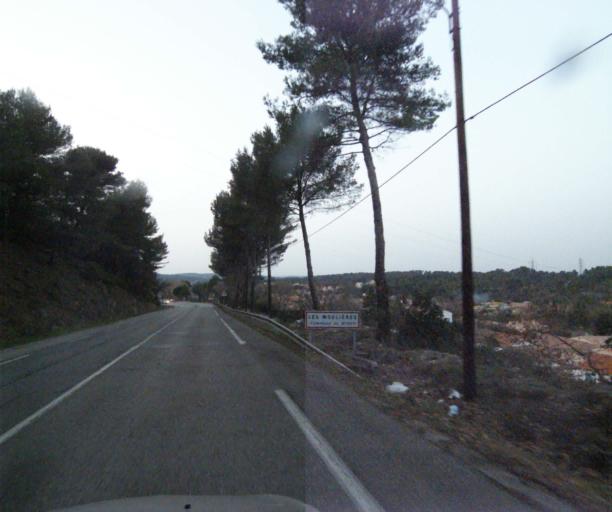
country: FR
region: Provence-Alpes-Cote d'Azur
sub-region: Departement des Bouches-du-Rhone
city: Gardanne
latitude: 43.4262
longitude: 5.4760
